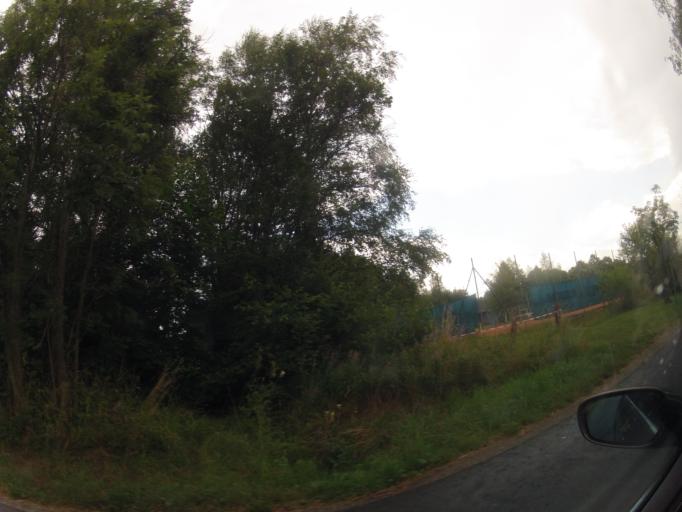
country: DE
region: Bavaria
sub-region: Upper Franconia
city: Weissenstadt
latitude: 50.1082
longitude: 11.8782
